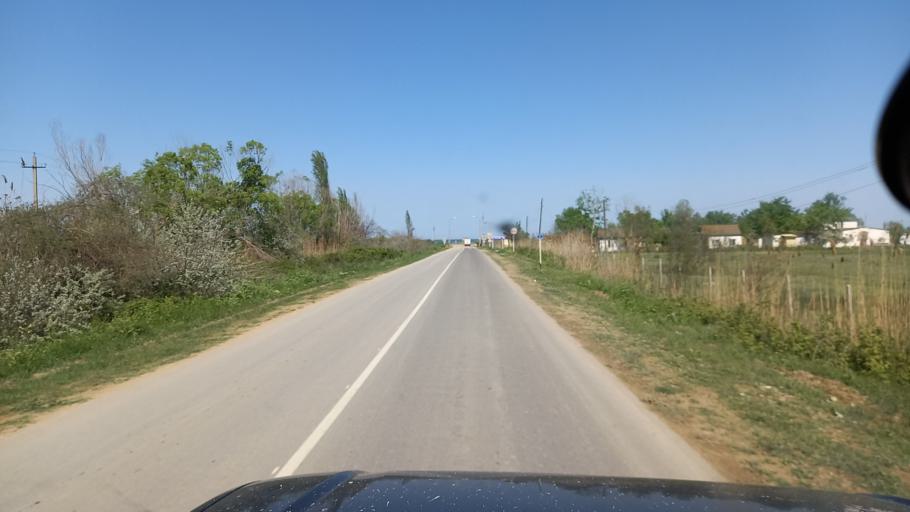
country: RU
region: Dagestan
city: Khazar
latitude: 41.9503
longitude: 48.3592
